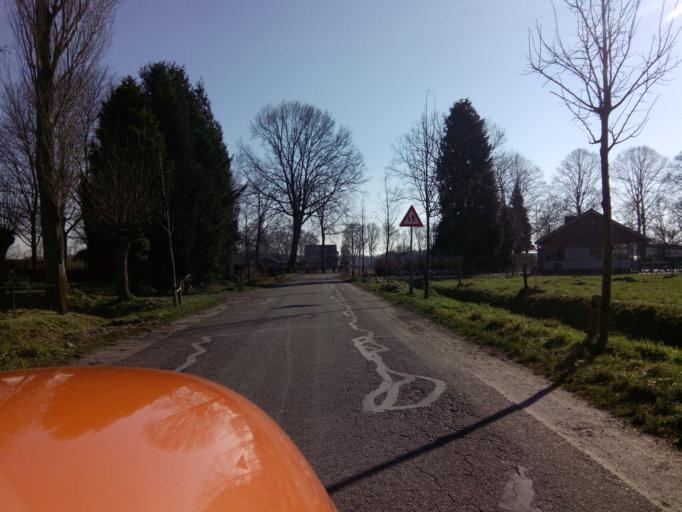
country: NL
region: Gelderland
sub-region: Gemeente Barneveld
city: Terschuur
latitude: 52.1148
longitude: 5.5117
